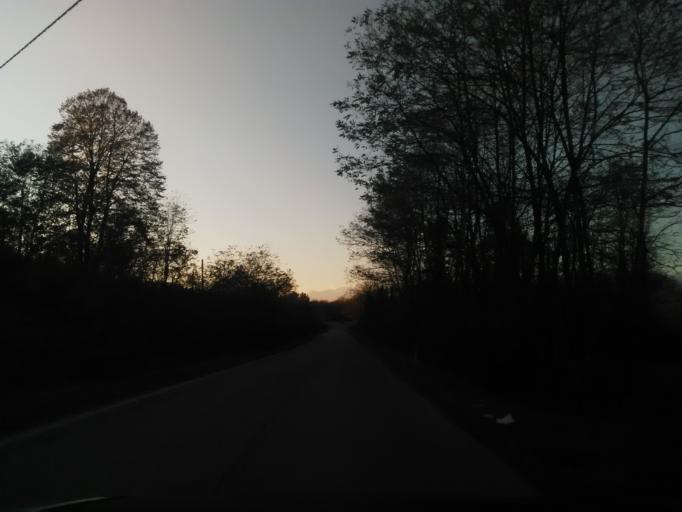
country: IT
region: Piedmont
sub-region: Provincia di Biella
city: Cerrione
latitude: 45.4638
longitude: 8.0725
